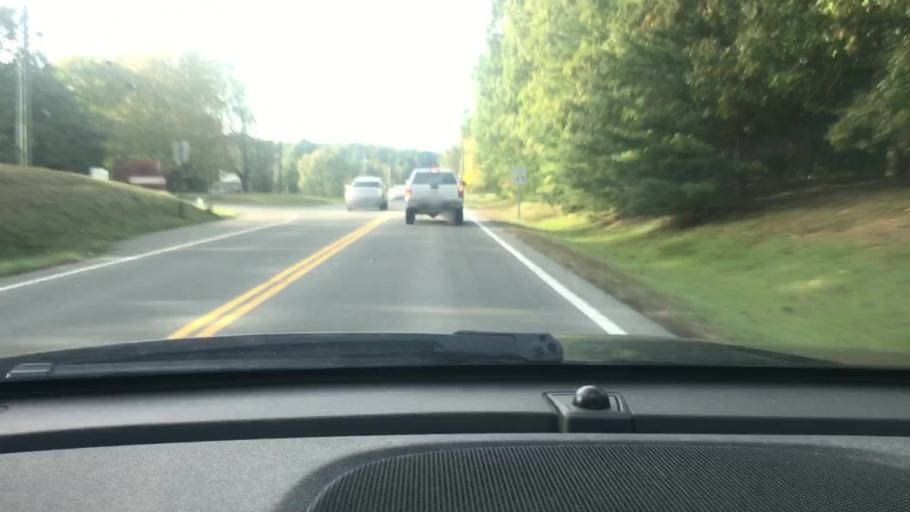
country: US
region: Tennessee
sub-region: Williamson County
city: Fairview
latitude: 35.9883
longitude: -87.1209
